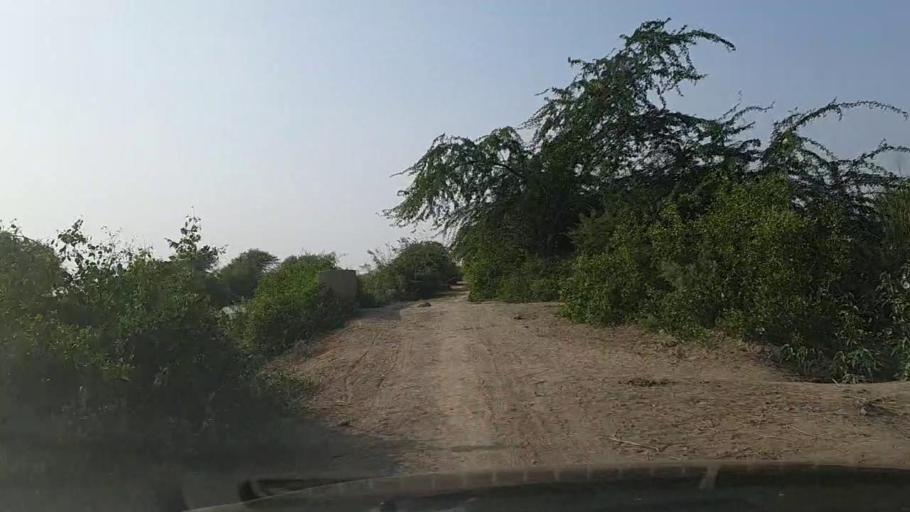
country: PK
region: Sindh
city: Mirpur Batoro
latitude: 24.6483
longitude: 68.2772
